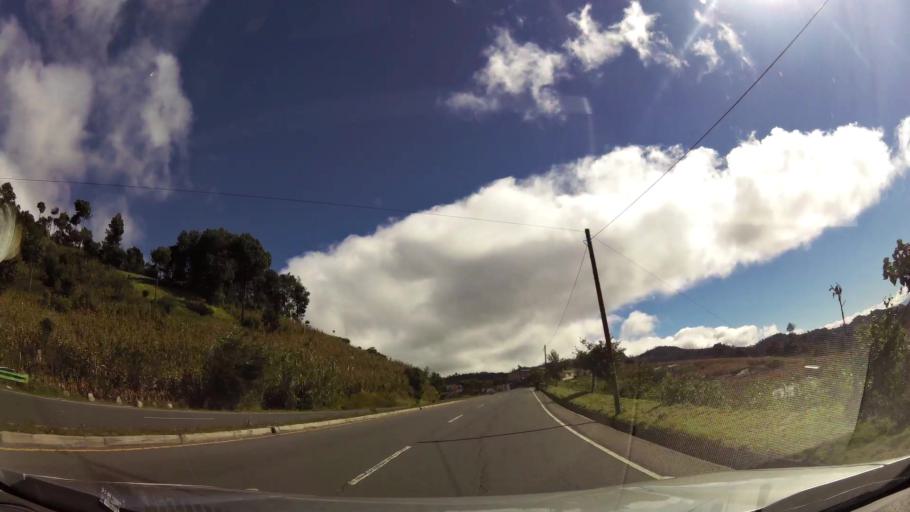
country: GT
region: Solola
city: Concepcion
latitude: 14.8356
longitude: -91.1826
